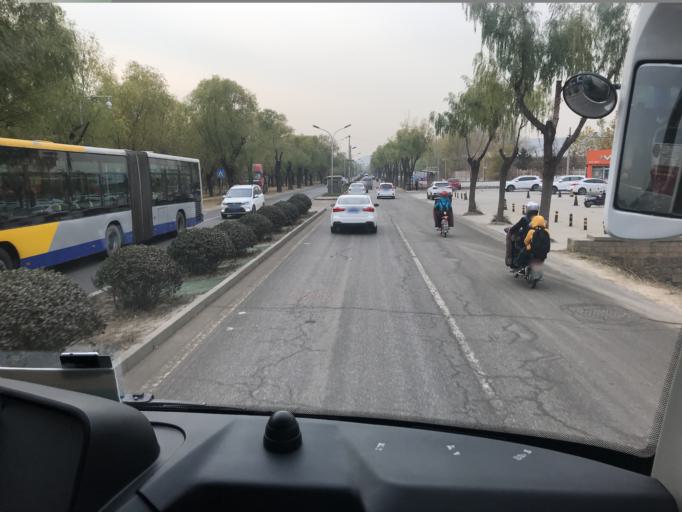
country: CN
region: Beijing
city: Wenquan
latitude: 40.0893
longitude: 116.2098
